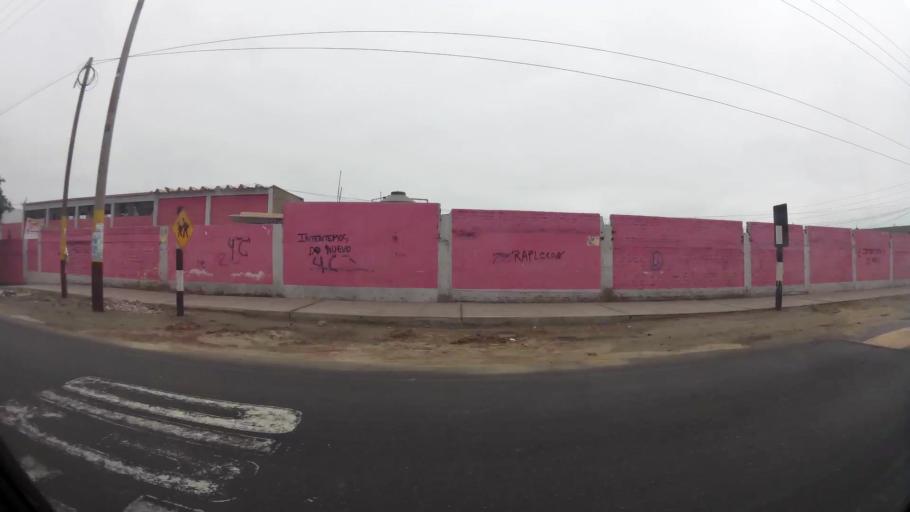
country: PE
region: Ancash
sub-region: Provincia de Santa
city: Chimbote
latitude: -9.0802
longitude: -78.5818
